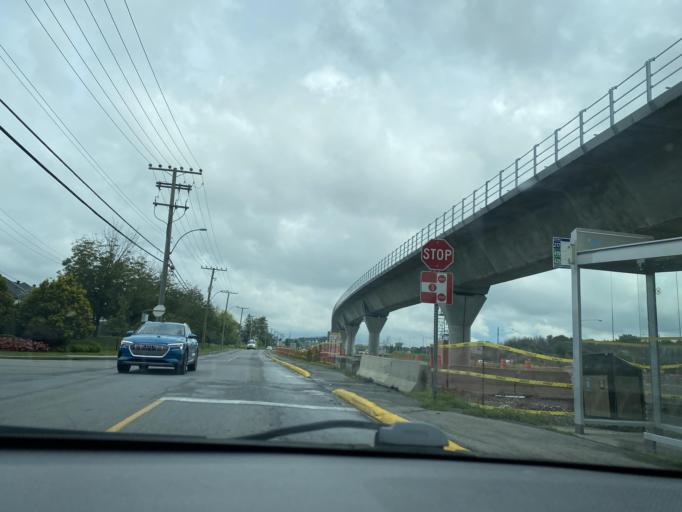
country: CA
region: Quebec
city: Beaconsfield
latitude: 45.4374
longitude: -73.8952
